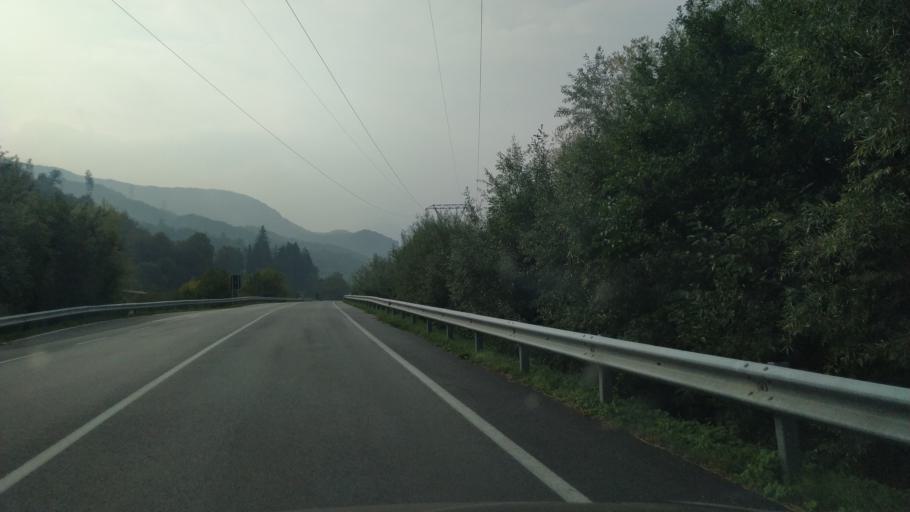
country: IT
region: Piedmont
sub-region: Provincia di Cuneo
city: Robilante
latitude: 44.2927
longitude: 7.5177
